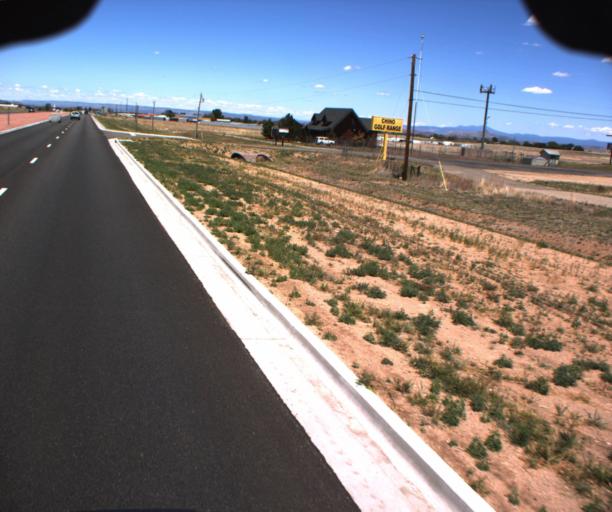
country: US
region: Arizona
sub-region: Yavapai County
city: Chino Valley
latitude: 34.7066
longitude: -112.4507
